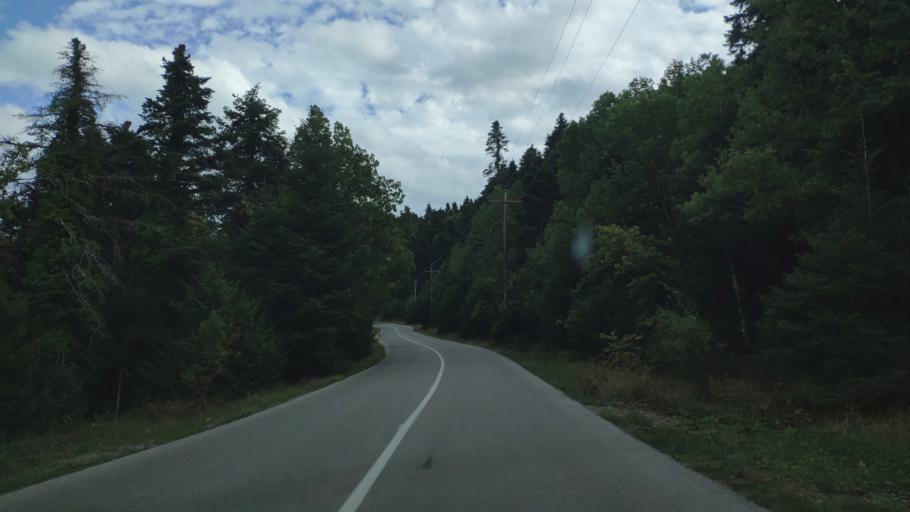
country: GR
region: Central Greece
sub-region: Nomos Fthiotidos
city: Anthili
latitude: 38.7378
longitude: 22.3807
